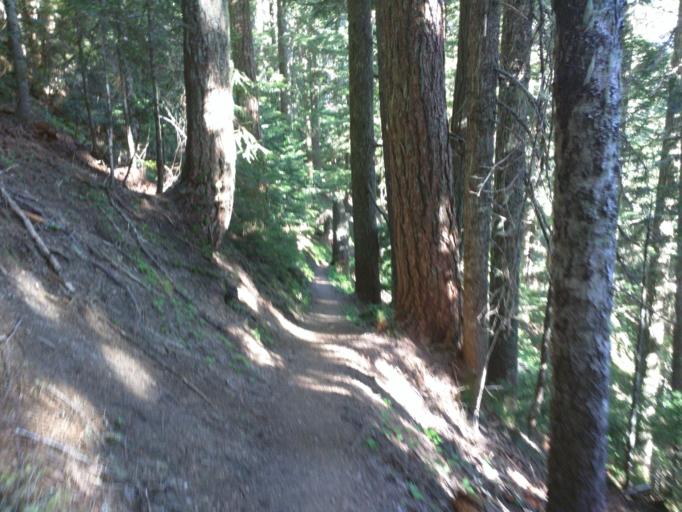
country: CA
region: British Columbia
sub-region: Fraser Valley Regional District
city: Chilliwack
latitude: 48.9200
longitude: -121.8563
